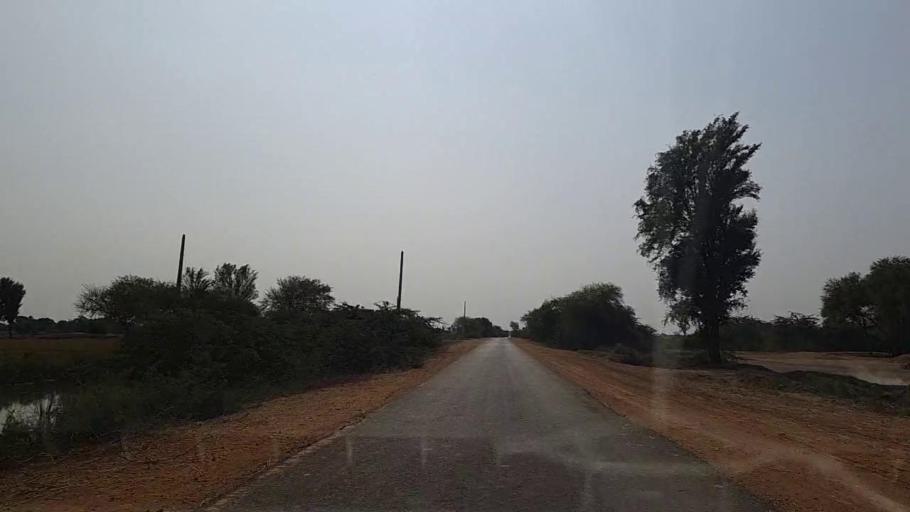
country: PK
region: Sindh
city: Chuhar Jamali
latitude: 24.3166
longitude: 67.9402
